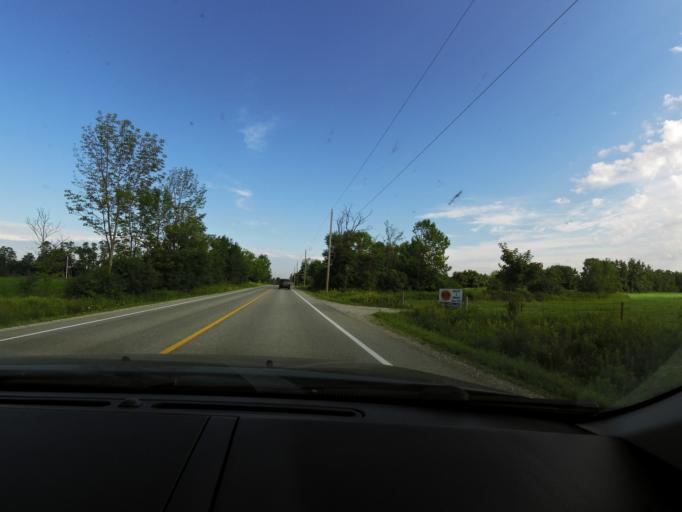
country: CA
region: Ontario
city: Brampton
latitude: 43.8148
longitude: -79.8633
